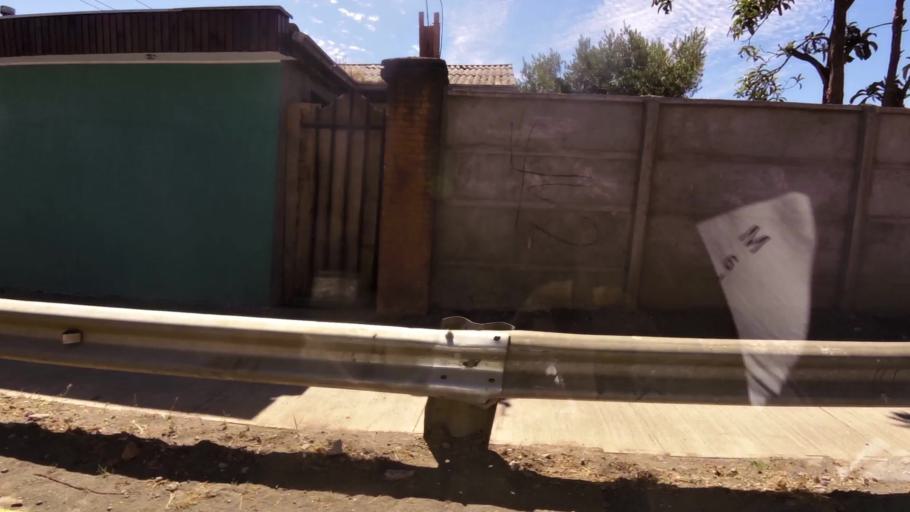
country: CL
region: Biobio
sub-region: Provincia de Concepcion
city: Penco
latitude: -36.7366
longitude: -72.9893
